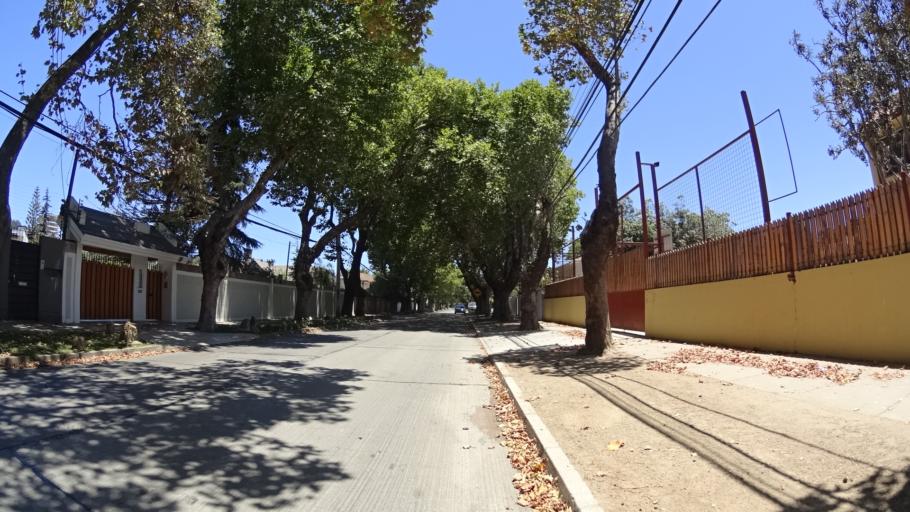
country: CL
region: Valparaiso
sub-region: Provincia de Valparaiso
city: Vina del Mar
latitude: -33.0306
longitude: -71.5300
